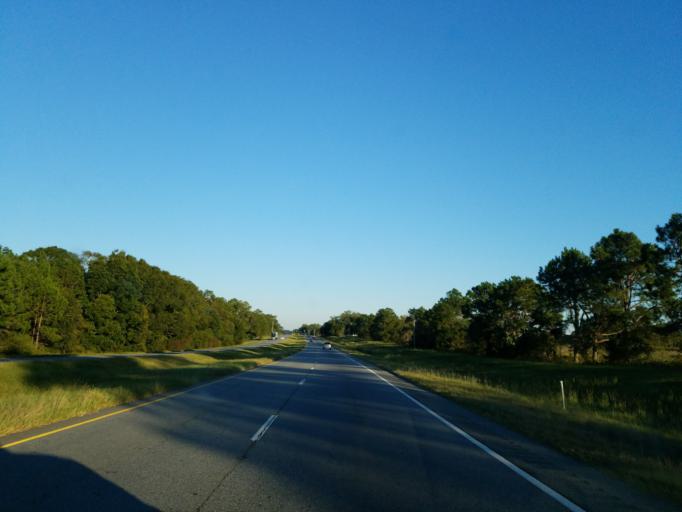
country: US
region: Georgia
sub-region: Worth County
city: Sylvester
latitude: 31.4825
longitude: -83.6924
